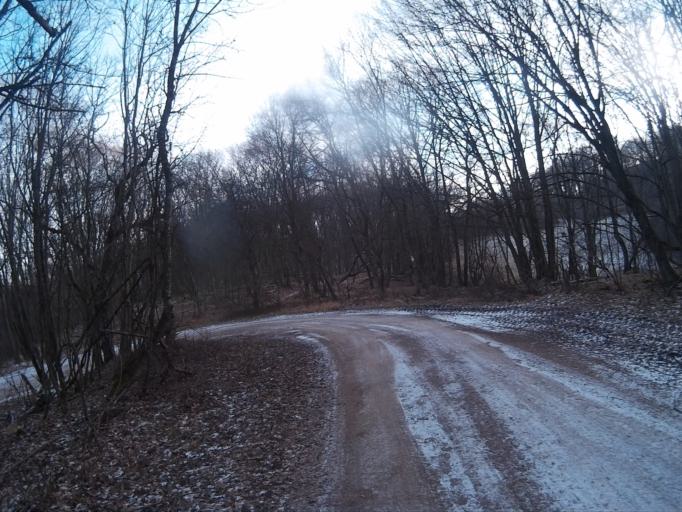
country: SK
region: Kosicky
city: Roznava
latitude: 48.5456
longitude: 20.6518
